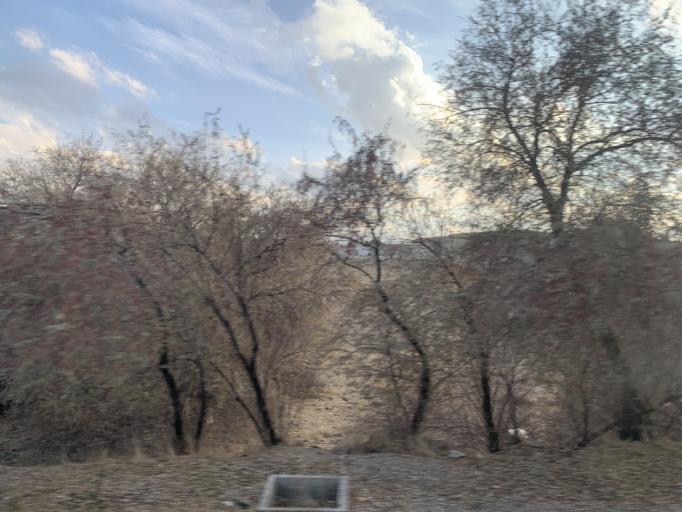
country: TR
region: Nevsehir
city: Avanos
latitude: 38.7045
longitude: 34.8348
